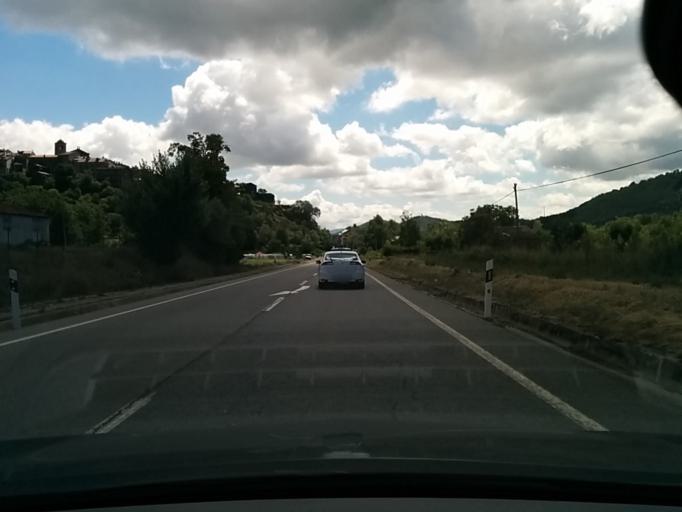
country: ES
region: Aragon
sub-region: Provincia de Huesca
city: Boltana
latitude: 42.4471
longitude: 0.0622
